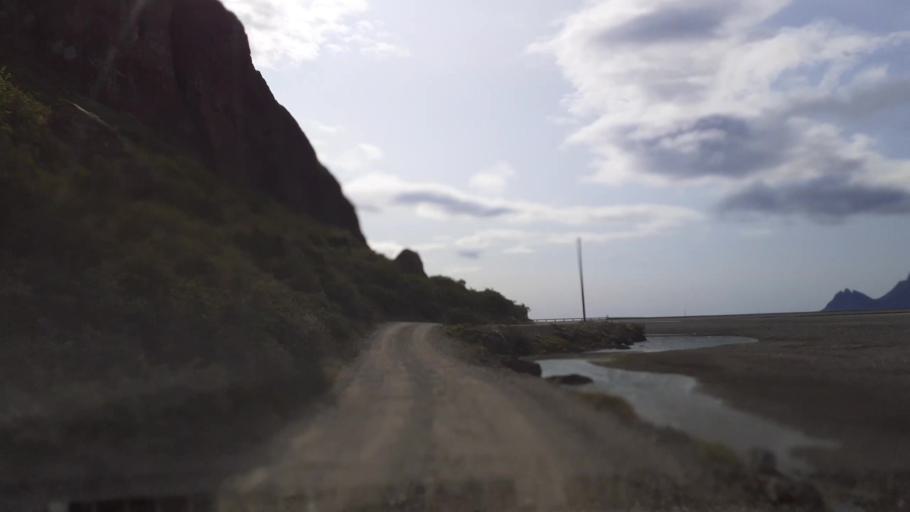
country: IS
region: East
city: Hoefn
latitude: 64.4324
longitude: -14.8915
